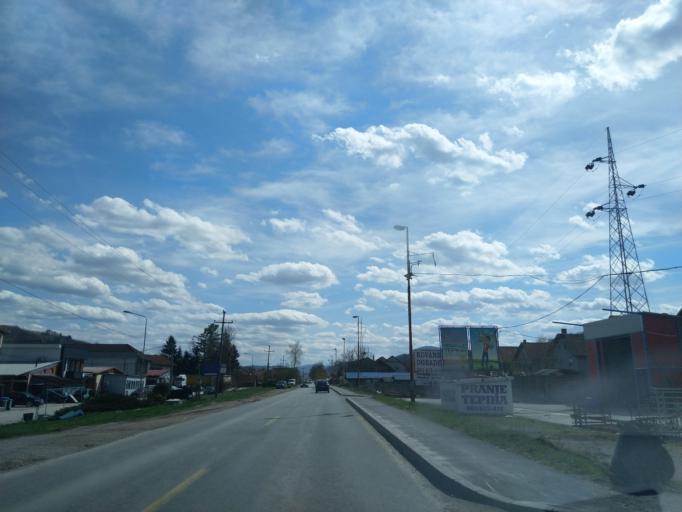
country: RS
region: Central Serbia
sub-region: Zlatiborski Okrug
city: Arilje
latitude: 43.7512
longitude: 20.1048
